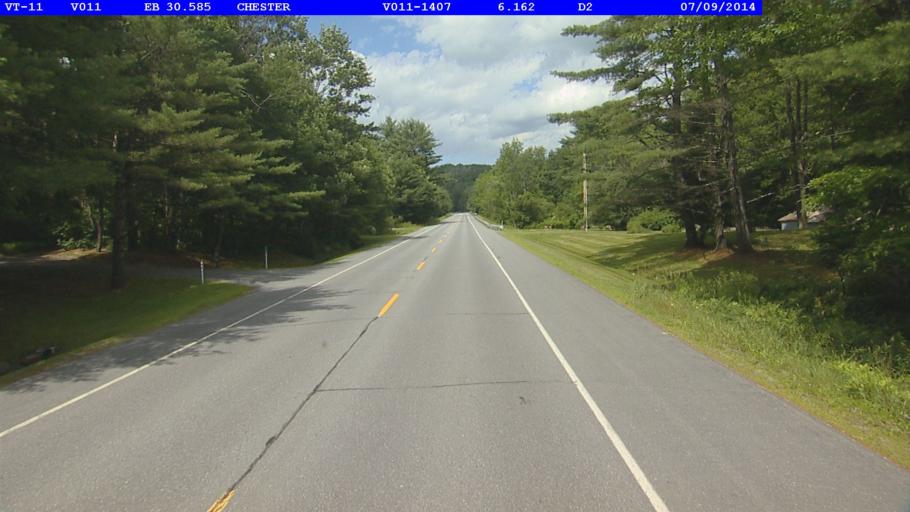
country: US
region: Vermont
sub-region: Windsor County
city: Chester
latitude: 43.2674
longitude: -72.5743
